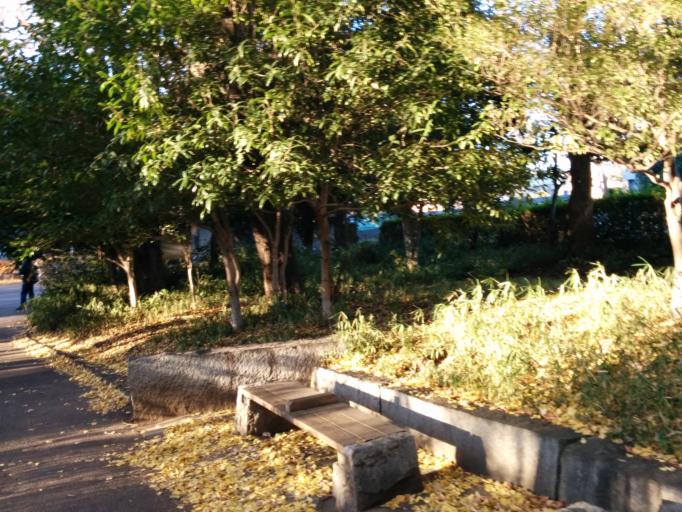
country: JP
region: Tokyo
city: Tokyo
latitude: 35.6517
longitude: 139.7274
